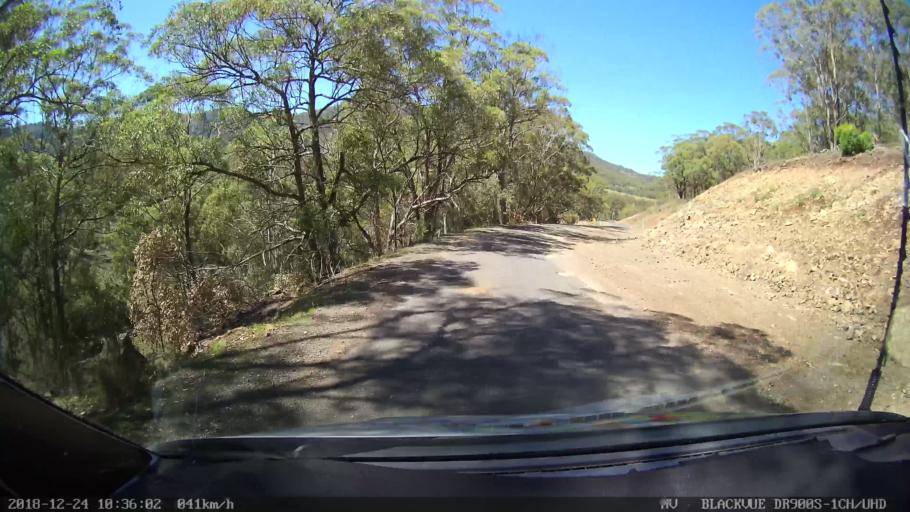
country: AU
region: New South Wales
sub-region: Upper Hunter Shire
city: Merriwa
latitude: -31.8421
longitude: 150.5010
